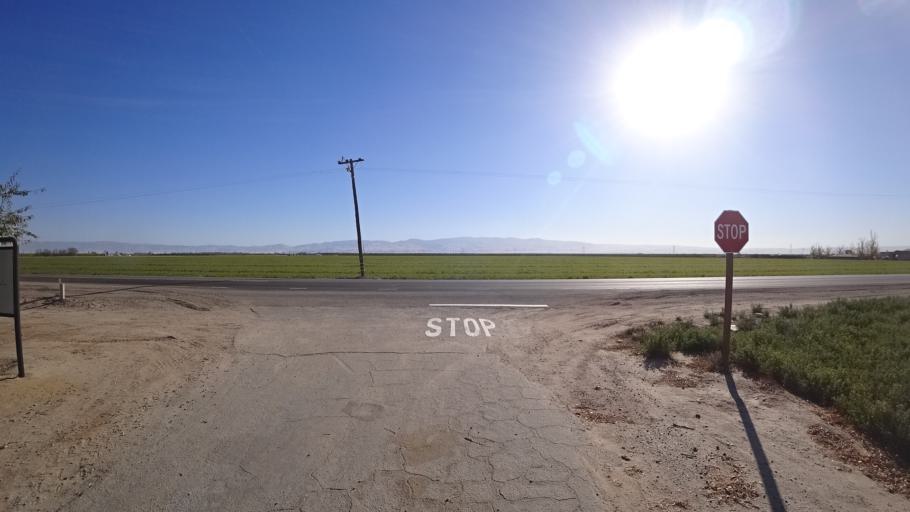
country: US
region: California
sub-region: Kern County
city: Greenfield
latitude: 35.2673
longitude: -119.1186
